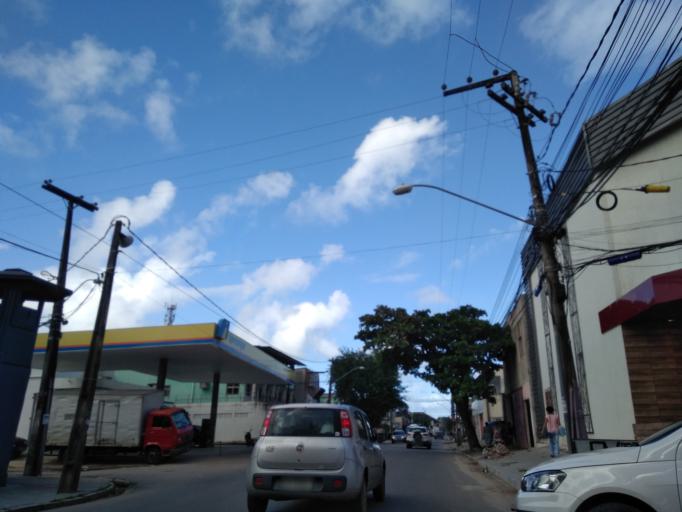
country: BR
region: Pernambuco
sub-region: Recife
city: Recife
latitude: -8.0757
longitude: -34.9158
